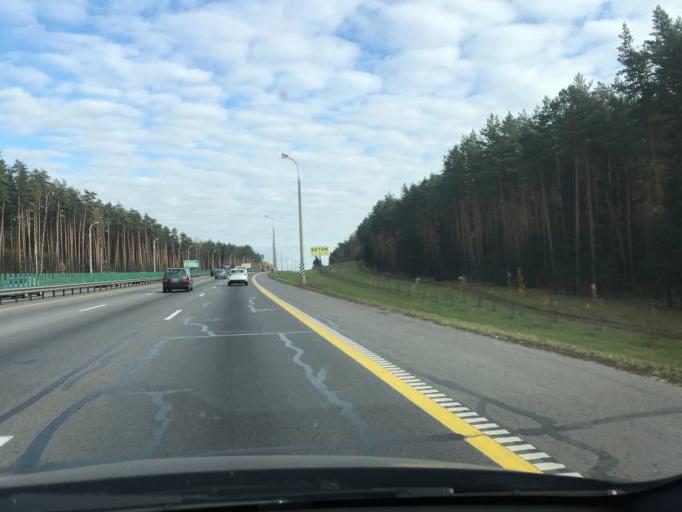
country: BY
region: Minsk
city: Syomkava
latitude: 53.9666
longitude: 27.4756
